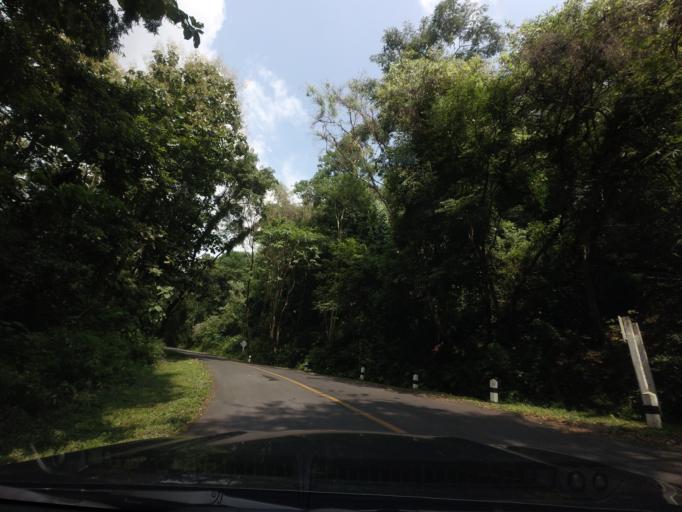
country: TH
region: Nan
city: Pua
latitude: 19.1839
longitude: 100.9974
